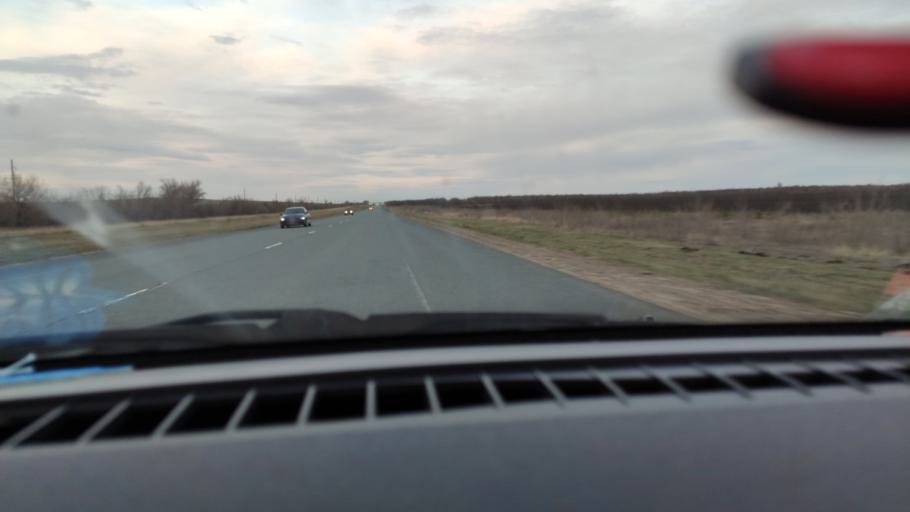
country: RU
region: Saratov
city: Yelshanka
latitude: 51.8280
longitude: 46.2636
